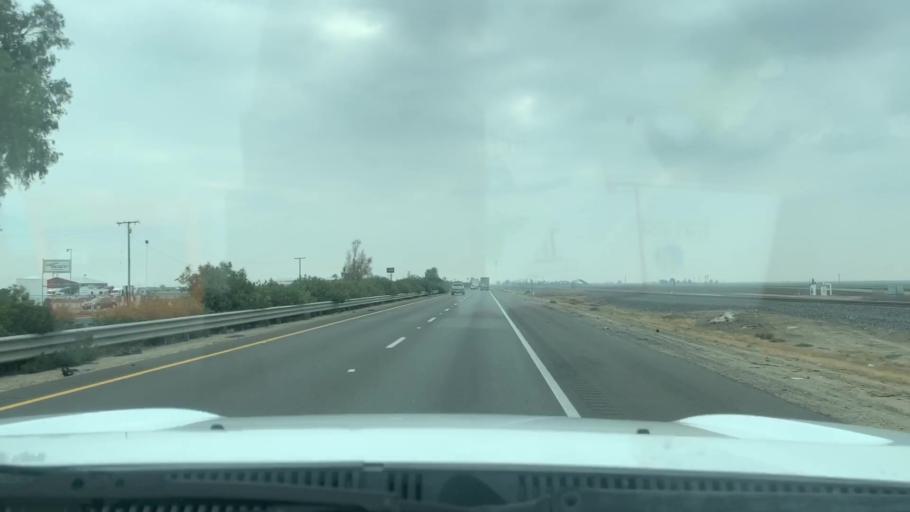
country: US
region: California
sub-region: Tulare County
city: Tipton
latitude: 36.0880
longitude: -119.3210
